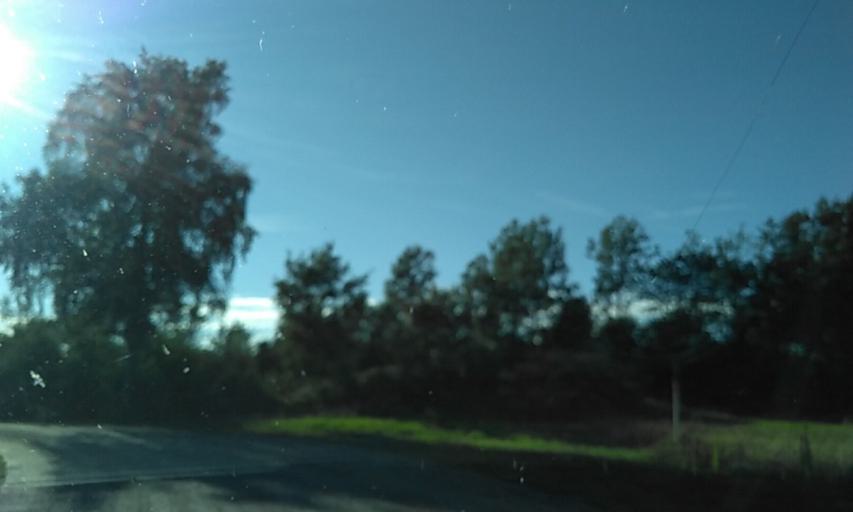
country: SE
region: Vaestra Goetaland
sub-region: Vara Kommun
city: Vara
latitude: 58.3696
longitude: 12.8463
